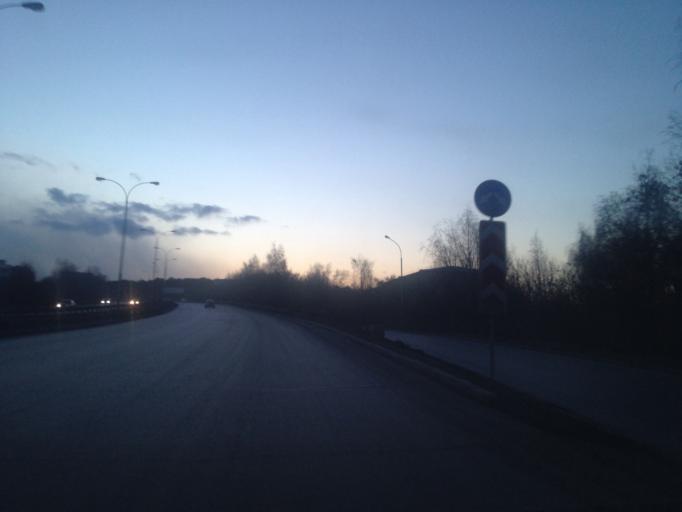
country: RU
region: Sverdlovsk
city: Yekaterinburg
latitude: 56.7906
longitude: 60.6112
